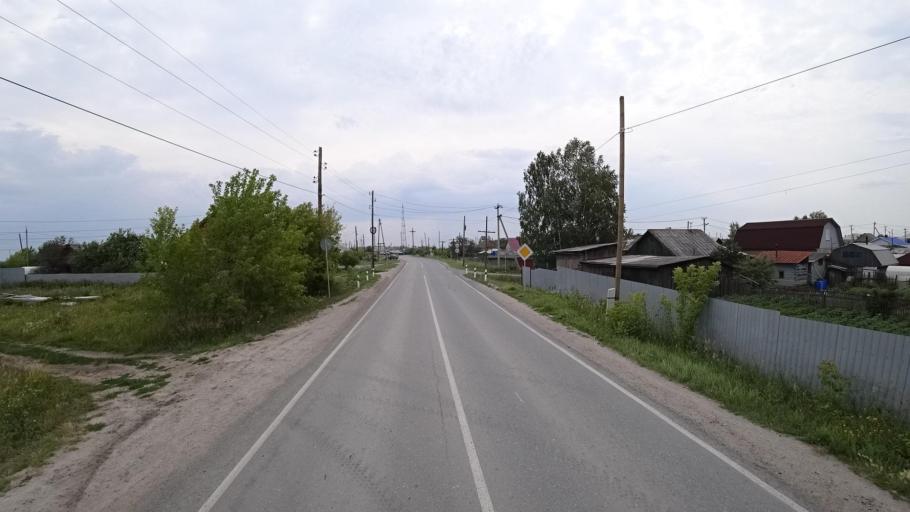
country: RU
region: Sverdlovsk
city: Kamyshlov
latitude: 56.8517
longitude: 62.7403
